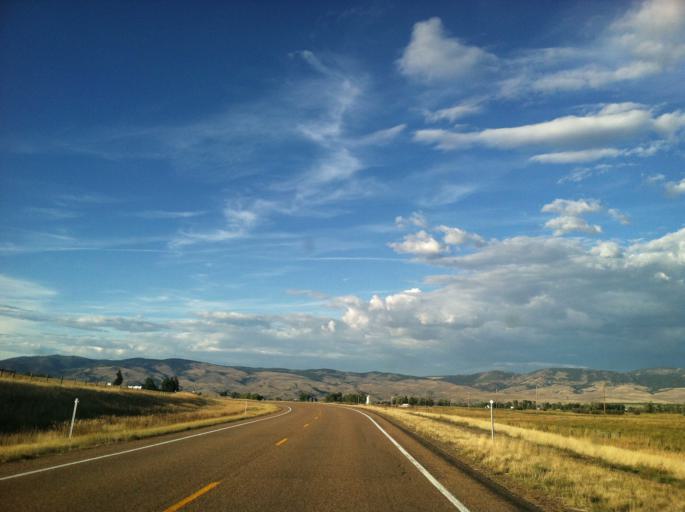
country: US
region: Montana
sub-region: Granite County
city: Philipsburg
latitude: 46.6016
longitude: -113.1869
